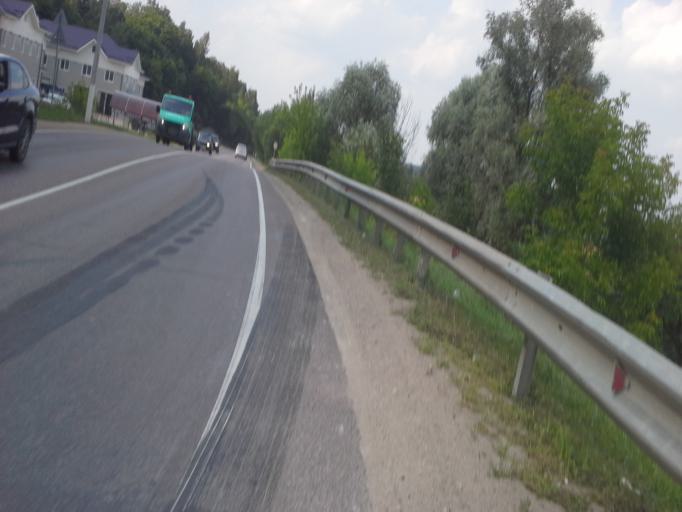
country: RU
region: Moskovskaya
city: Istra
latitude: 55.9005
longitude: 36.8085
